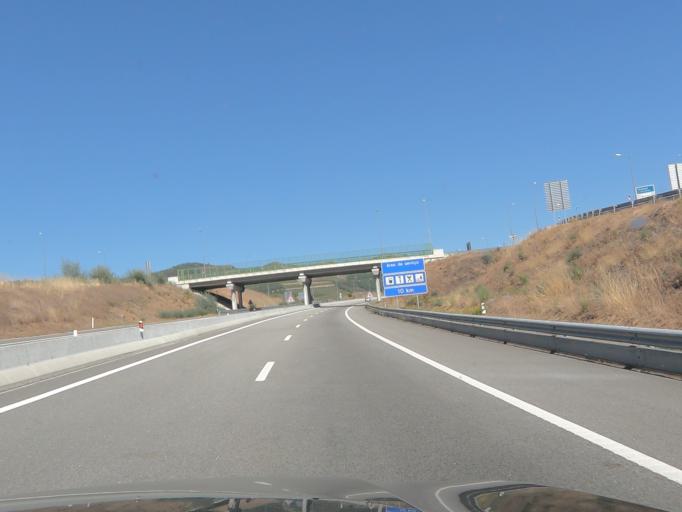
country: PT
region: Vila Real
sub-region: Murca
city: Murca
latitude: 41.4172
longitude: -7.4111
